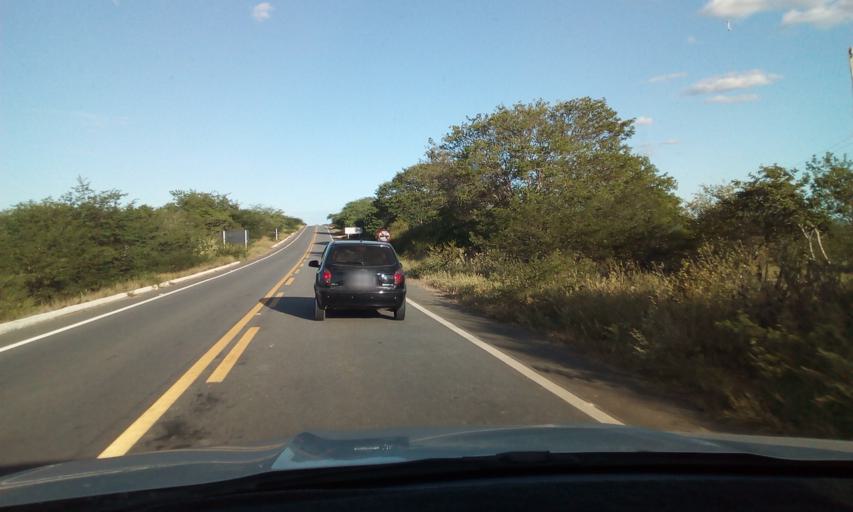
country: BR
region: Paraiba
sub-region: Cuite
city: Cuite
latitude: -6.7017
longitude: -36.0787
